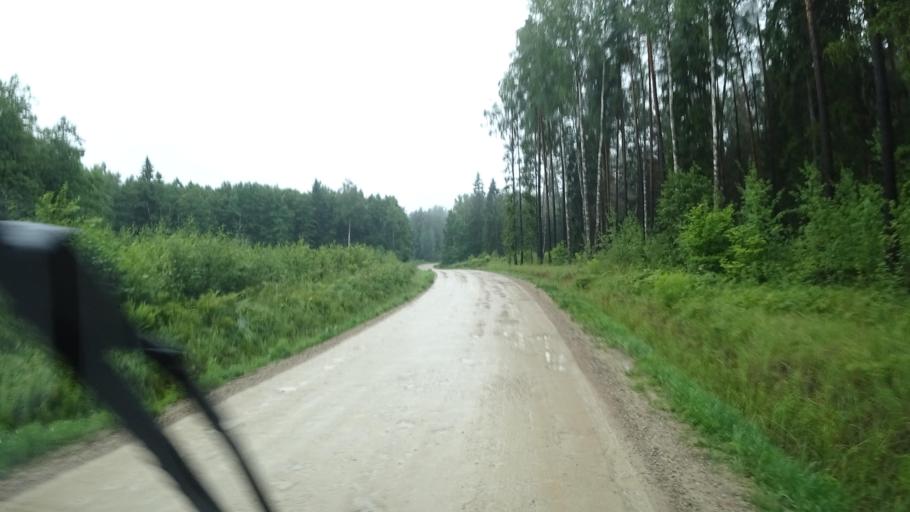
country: LV
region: Lecava
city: Iecava
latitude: 56.6534
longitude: 24.1746
